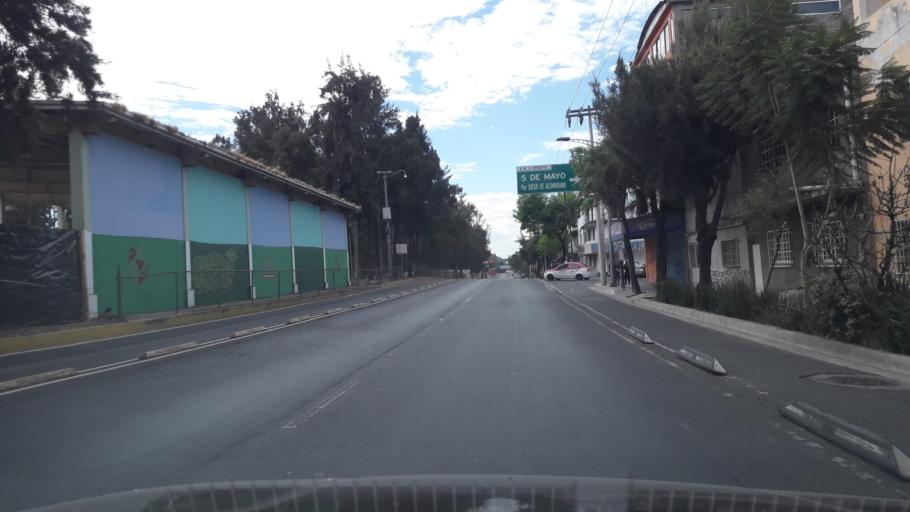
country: MX
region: Mexico City
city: Gustavo A. Madero
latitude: 19.4965
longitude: -99.0908
